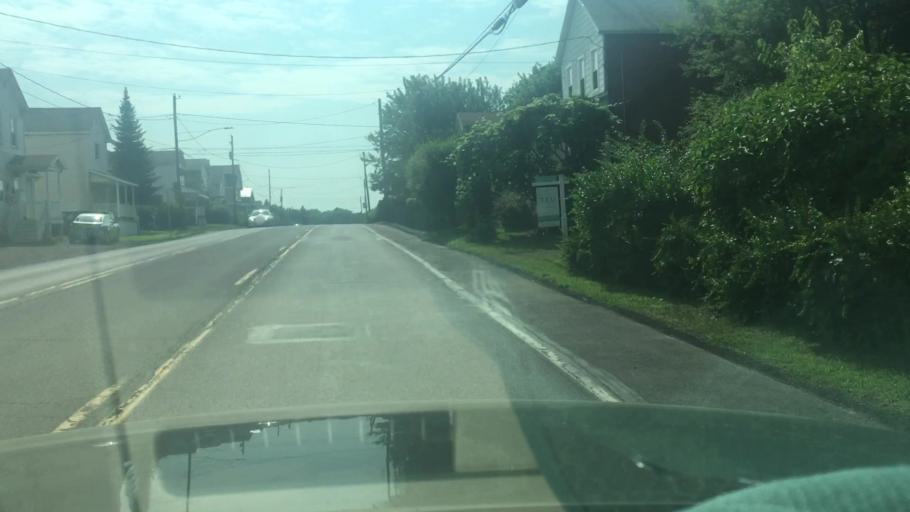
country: US
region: Pennsylvania
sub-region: Northumberland County
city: Kulpmont
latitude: 40.8176
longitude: -76.4638
